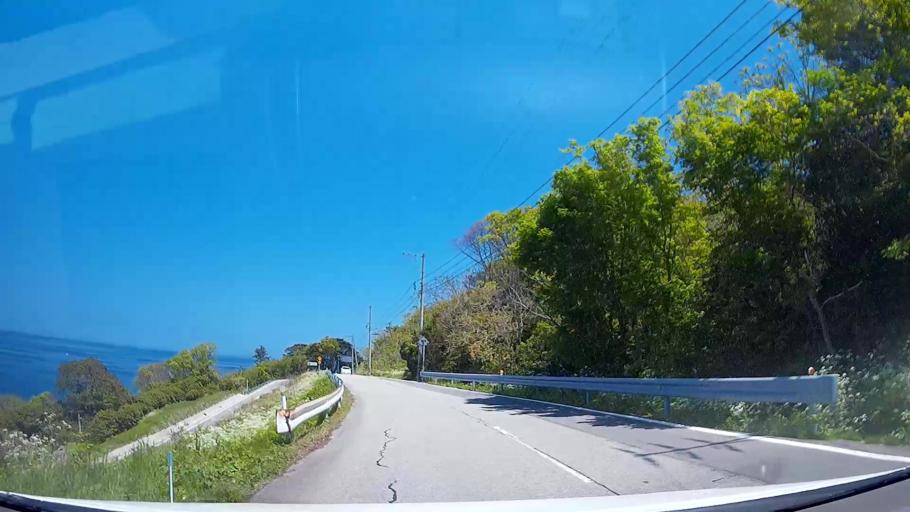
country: JP
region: Ishikawa
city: Nanao
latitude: 37.5269
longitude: 137.2684
